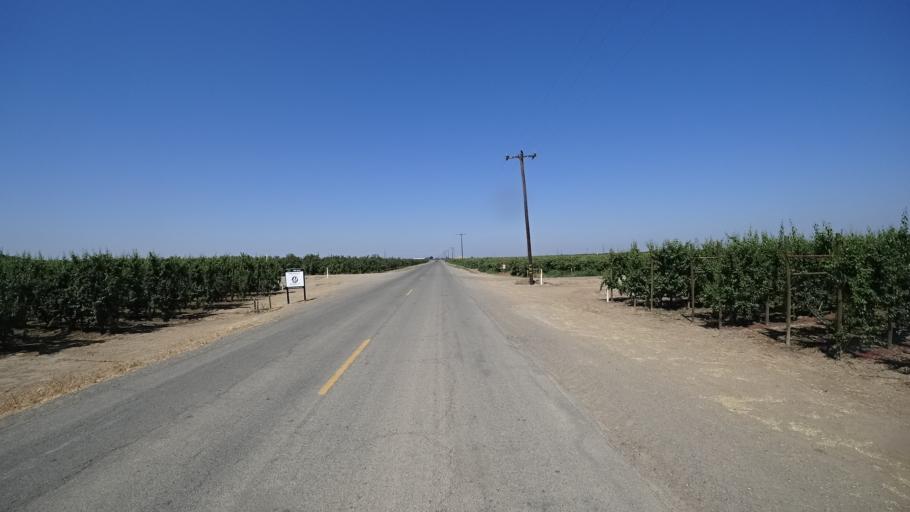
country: US
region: California
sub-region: Kings County
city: Hanford
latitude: 36.3719
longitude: -119.5780
